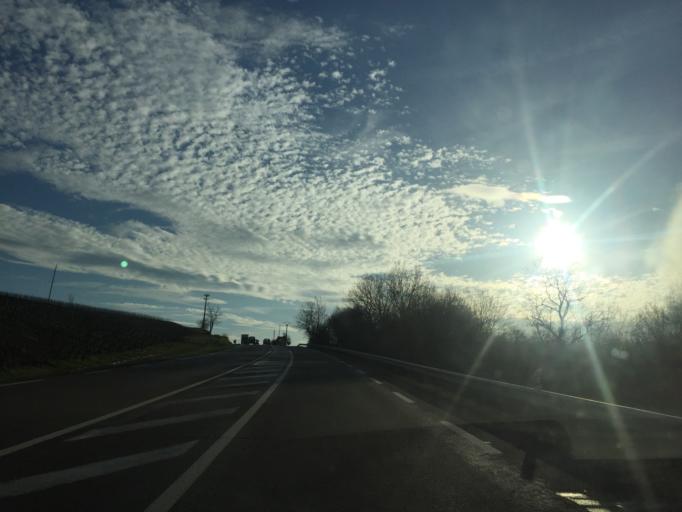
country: FR
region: Franche-Comte
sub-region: Departement du Jura
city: Arbois
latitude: 46.9339
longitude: 5.7763
